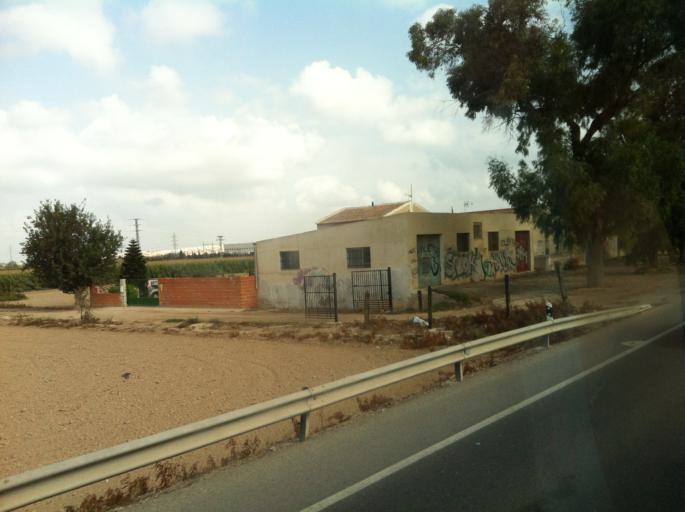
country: ES
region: Valencia
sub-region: Provincia de Alicante
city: Guardamar del Segura
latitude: 38.1050
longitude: -0.6619
